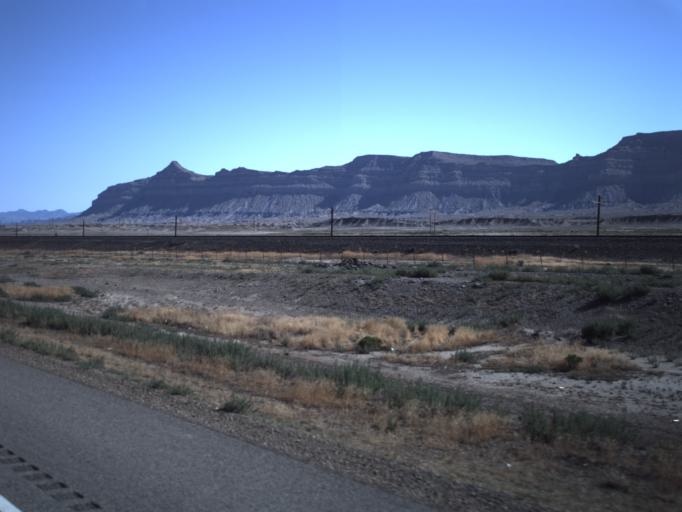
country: US
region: Utah
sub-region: Carbon County
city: East Carbon City
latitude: 39.1022
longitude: -110.3241
